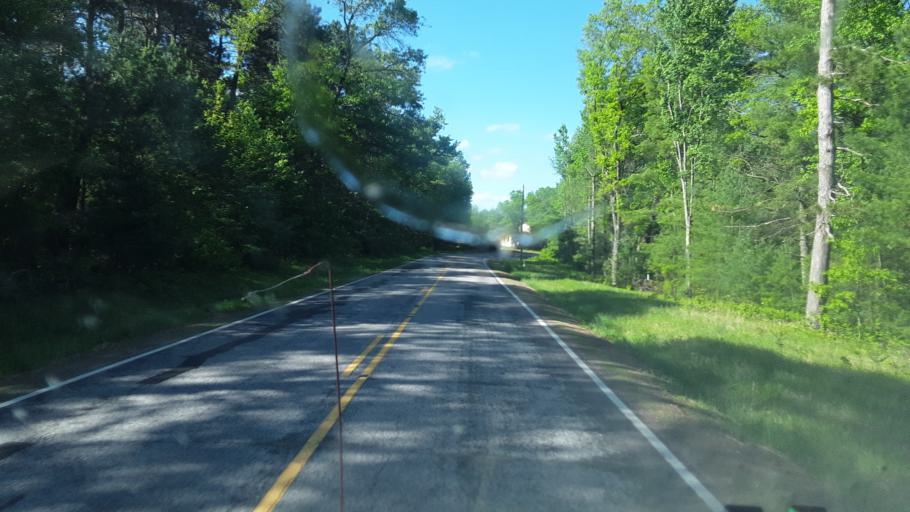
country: US
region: Wisconsin
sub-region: Wood County
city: Nekoosa
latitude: 44.3141
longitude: -90.1280
